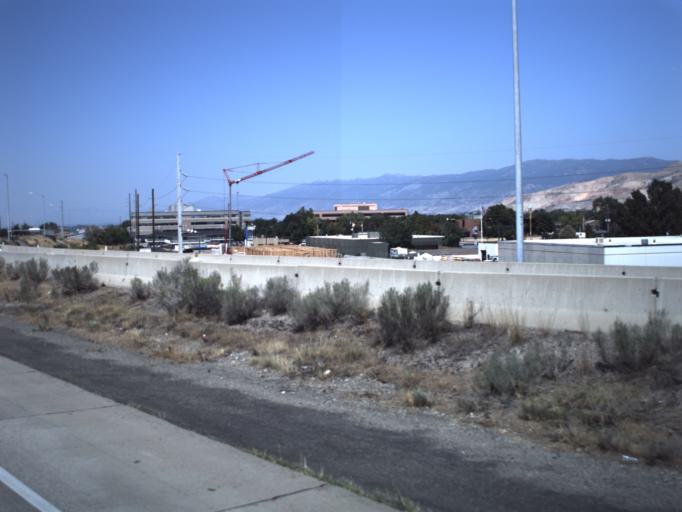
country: US
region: Utah
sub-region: Salt Lake County
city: Salt Lake City
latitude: 40.7686
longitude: -111.9487
